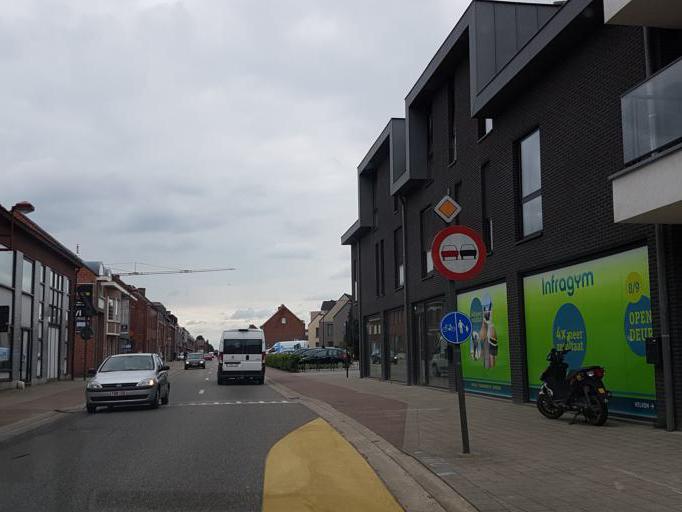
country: BE
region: Flanders
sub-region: Provincie Antwerpen
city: Rijkevorsel
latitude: 51.3470
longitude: 4.7592
